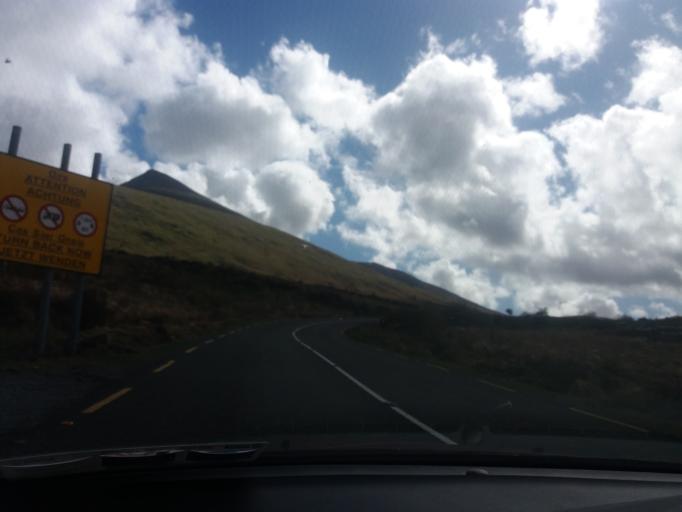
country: IE
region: Munster
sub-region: Ciarrai
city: Dingle
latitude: 52.2079
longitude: -10.1679
